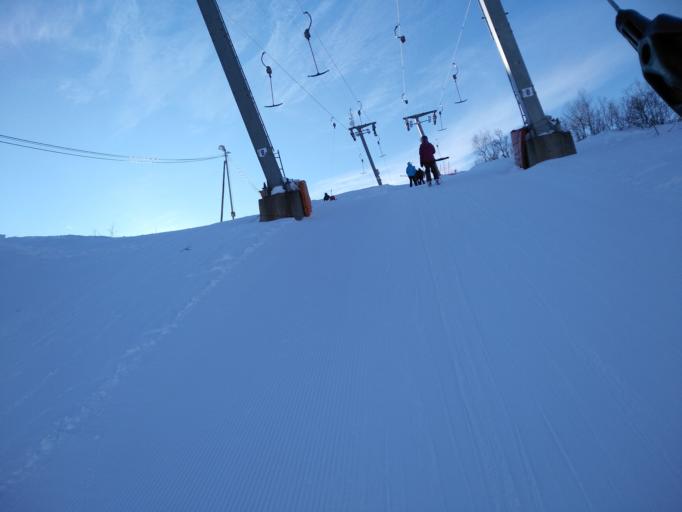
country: NO
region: Rogaland
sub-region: Sauda
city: Sauda
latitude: 59.6196
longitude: 6.2354
